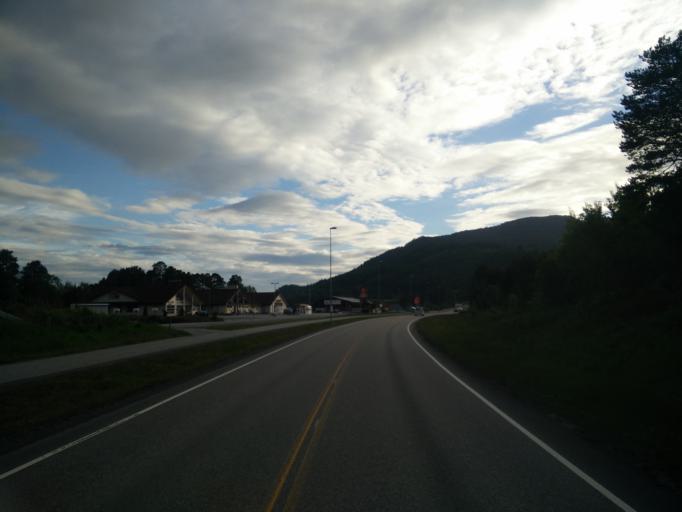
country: NO
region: More og Romsdal
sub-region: Kristiansund
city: Rensvik
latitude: 63.0124
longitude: 7.9796
